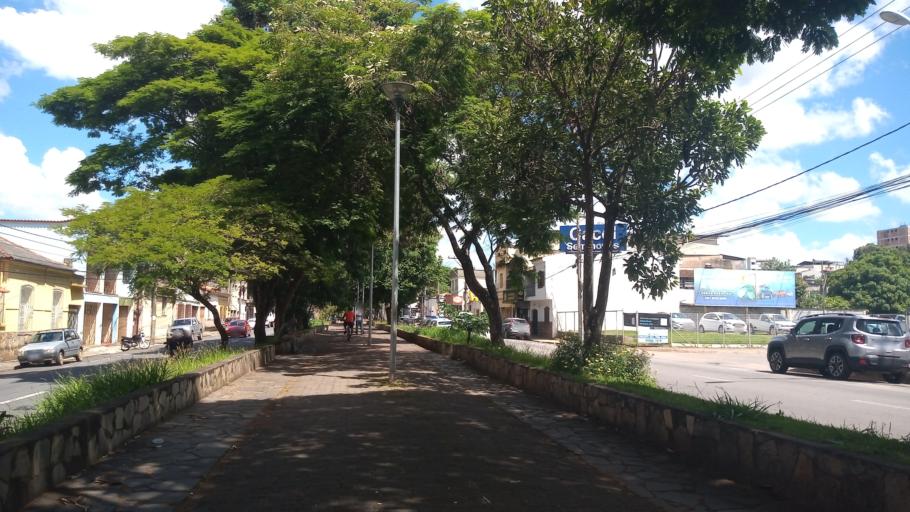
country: BR
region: Minas Gerais
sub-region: Sao Joao Del Rei
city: Sao Joao del Rei
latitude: -21.1241
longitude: -44.2478
